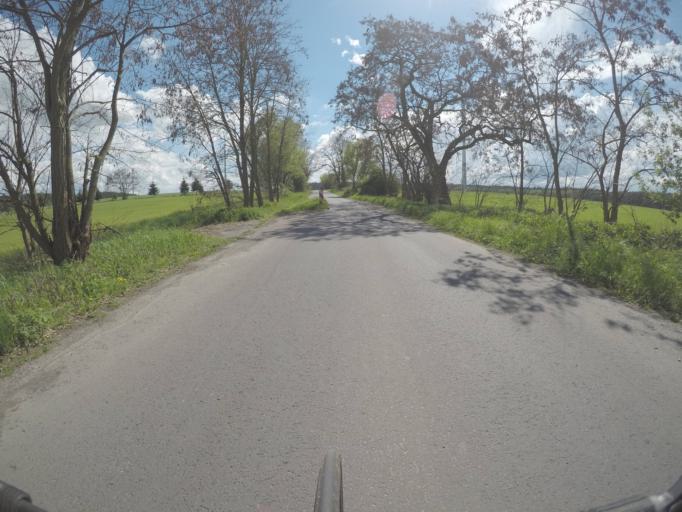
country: DE
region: Brandenburg
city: Rudnitz
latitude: 52.7210
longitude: 13.5951
